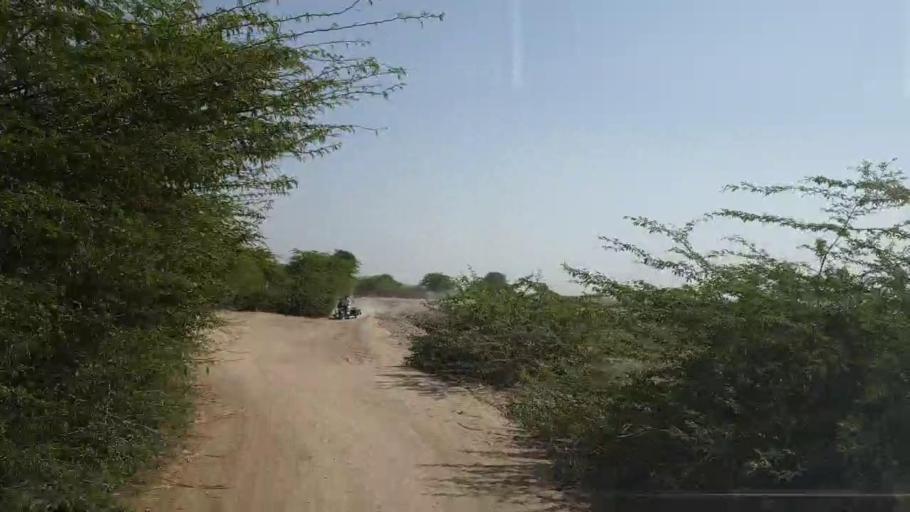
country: PK
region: Sindh
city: Naukot
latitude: 24.9745
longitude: 69.4934
